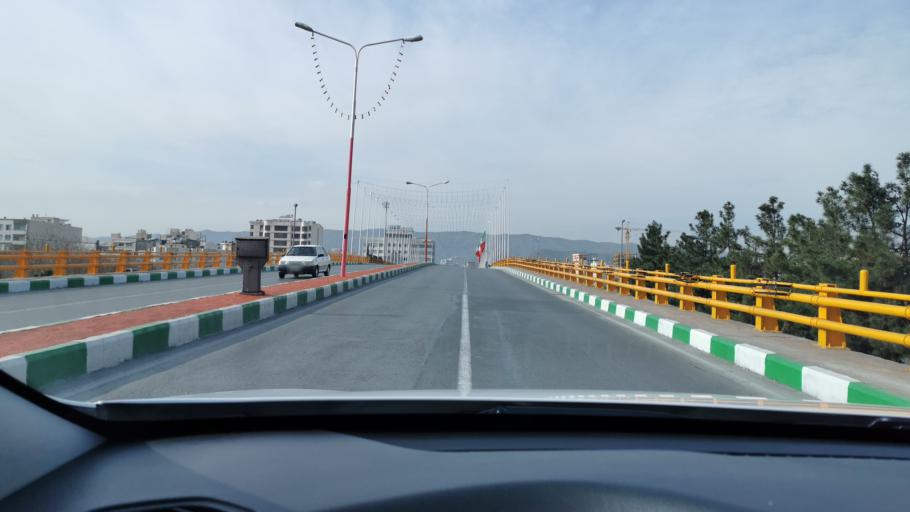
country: IR
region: Razavi Khorasan
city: Mashhad
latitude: 36.3240
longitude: 59.5164
